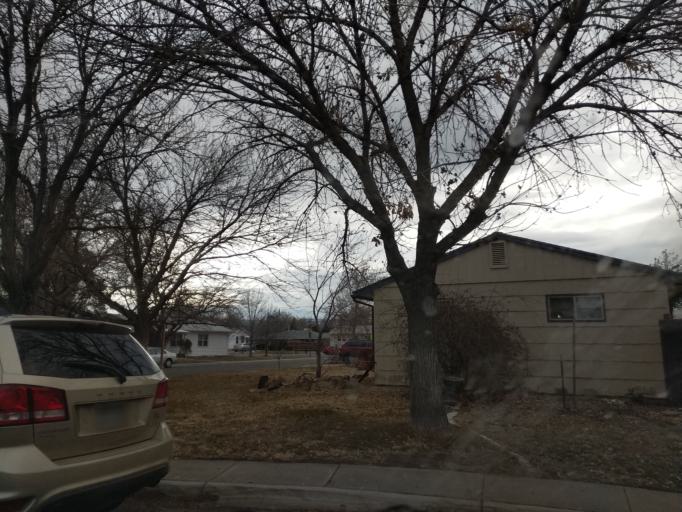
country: US
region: Colorado
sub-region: Mesa County
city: Grand Junction
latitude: 39.0725
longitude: -108.5424
